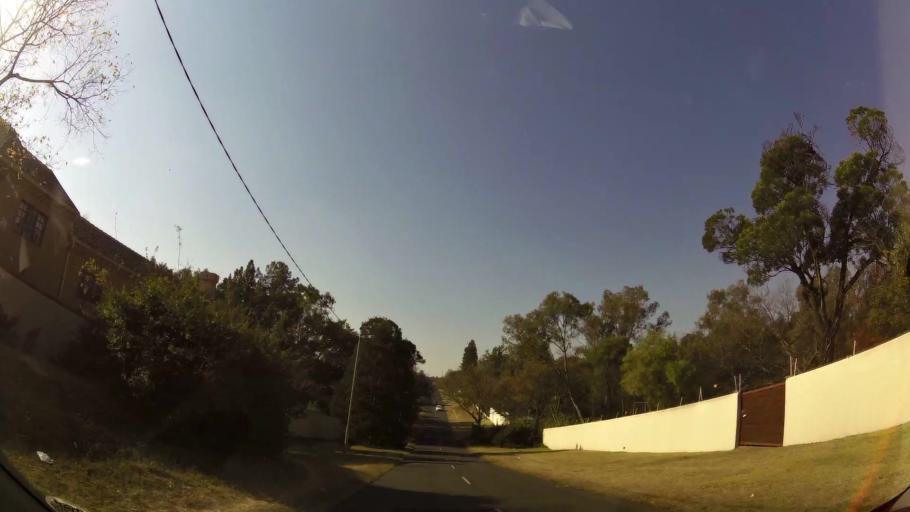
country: ZA
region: Gauteng
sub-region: City of Johannesburg Metropolitan Municipality
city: Diepsloot
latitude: -26.0661
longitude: 28.0085
